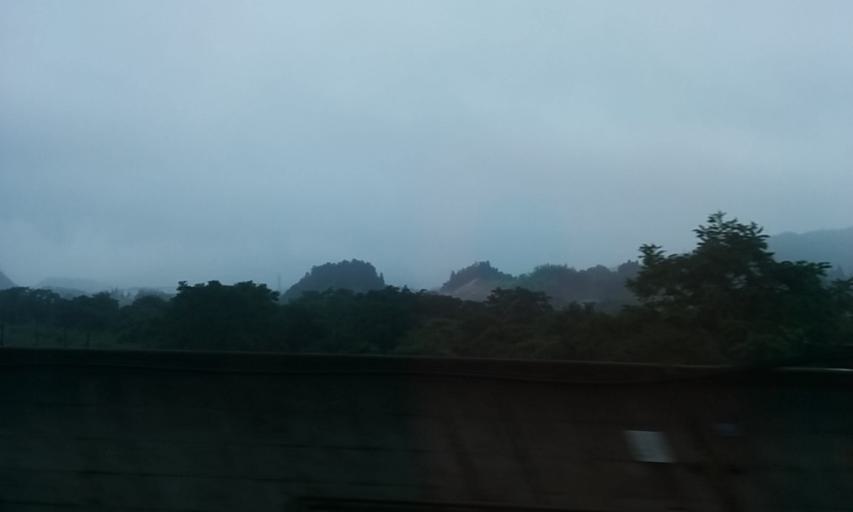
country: JP
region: Miyagi
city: Okawara
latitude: 38.0368
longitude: 140.6817
